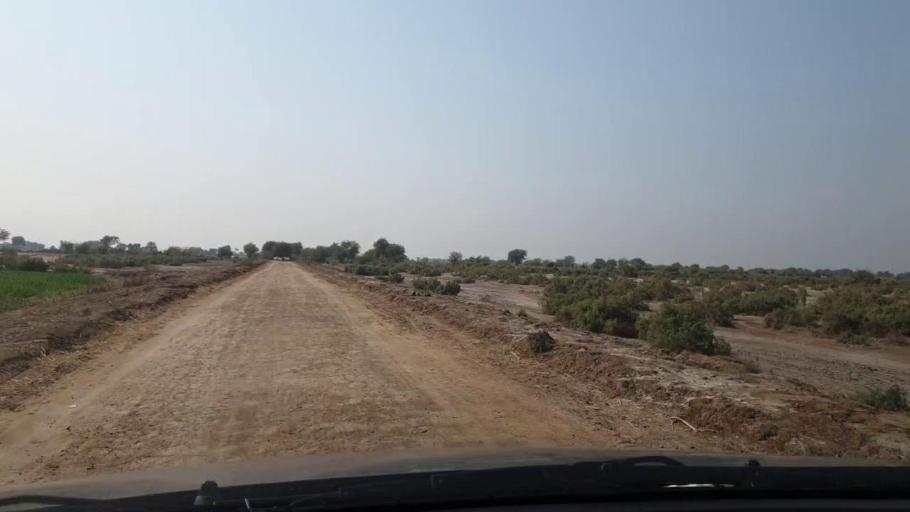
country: PK
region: Sindh
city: Jhol
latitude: 25.8874
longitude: 68.9982
